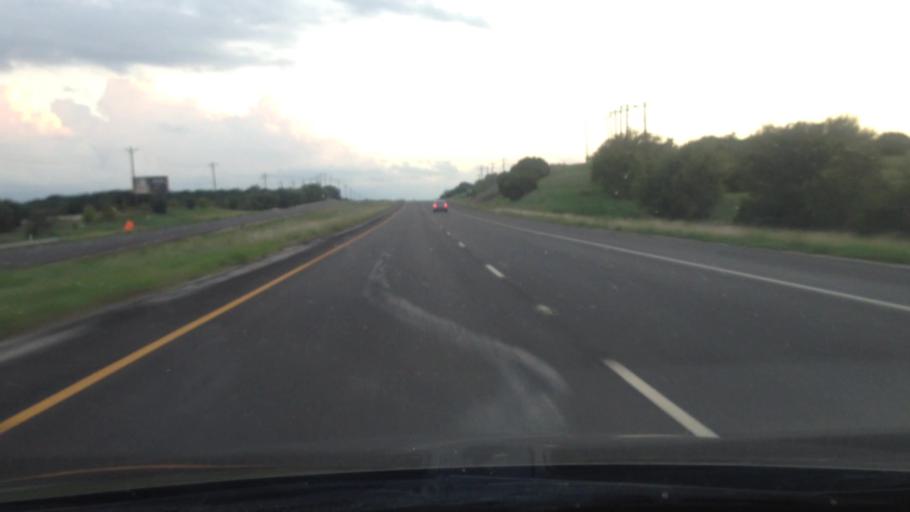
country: US
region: Texas
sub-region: Hood County
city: DeCordova
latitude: 32.5202
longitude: -97.6280
